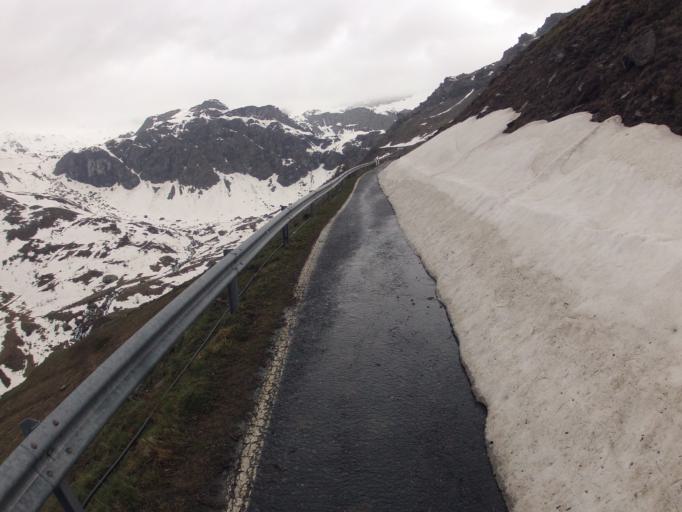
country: IT
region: Piedmont
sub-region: Provincia di Cuneo
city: Crissolo
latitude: 44.7033
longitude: 7.1128
